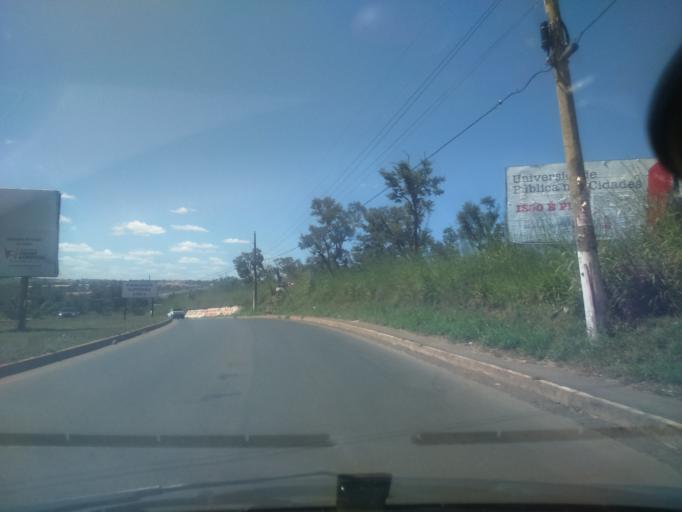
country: BR
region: Goias
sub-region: Luziania
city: Luziania
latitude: -16.1112
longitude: -47.9671
